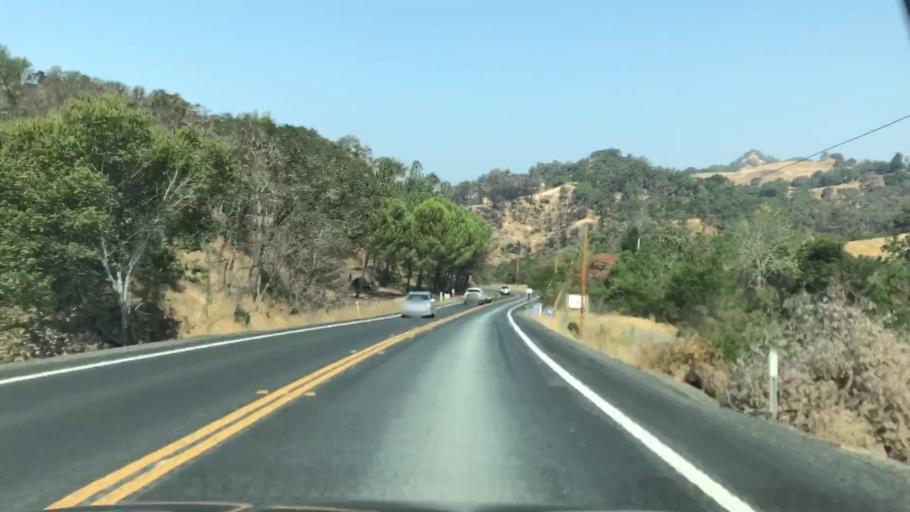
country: US
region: California
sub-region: Sonoma County
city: Larkfield-Wikiup
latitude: 38.5570
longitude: -122.6868
